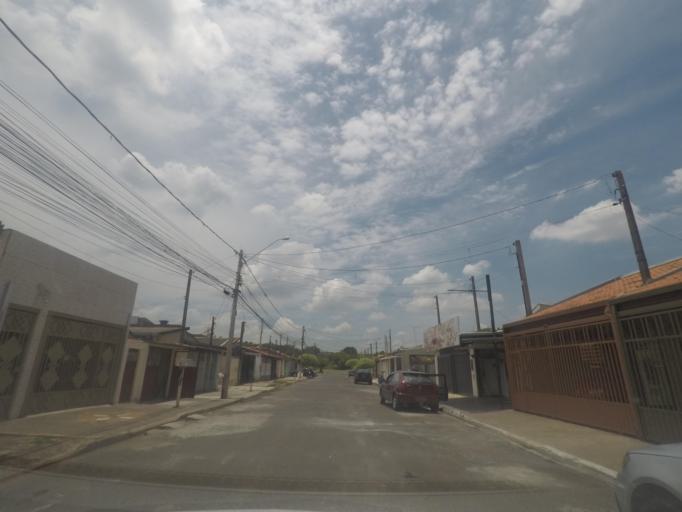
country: BR
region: Sao Paulo
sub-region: Nova Odessa
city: Nova Odessa
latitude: -22.7908
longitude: -47.2769
